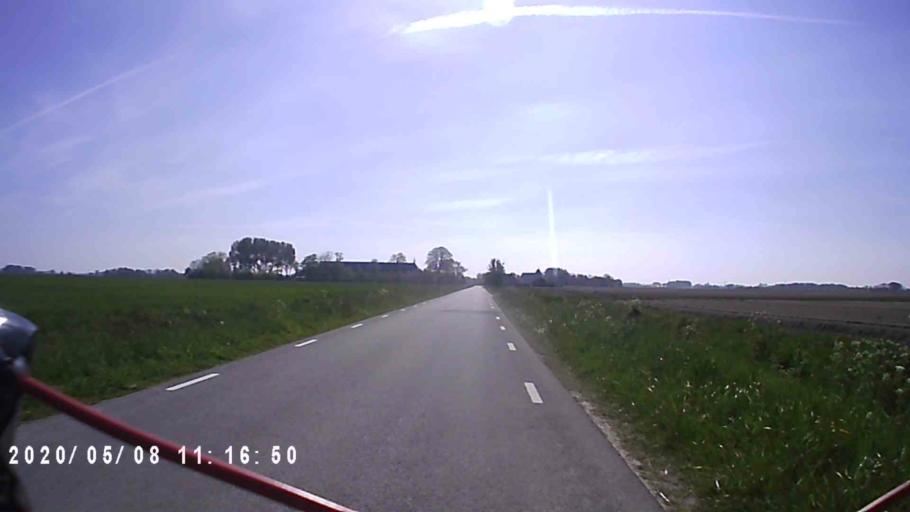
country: NL
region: Groningen
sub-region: Gemeente Bedum
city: Bedum
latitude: 53.3495
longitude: 6.6629
